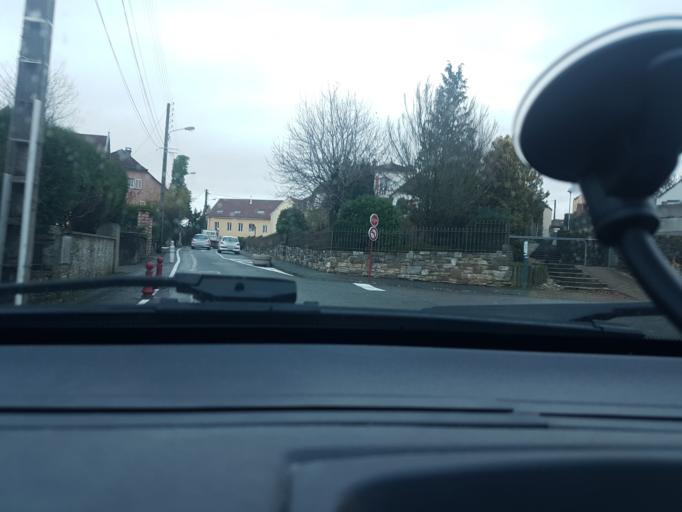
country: FR
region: Franche-Comte
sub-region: Territoire de Belfort
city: Bavilliers
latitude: 47.6217
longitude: 6.8342
